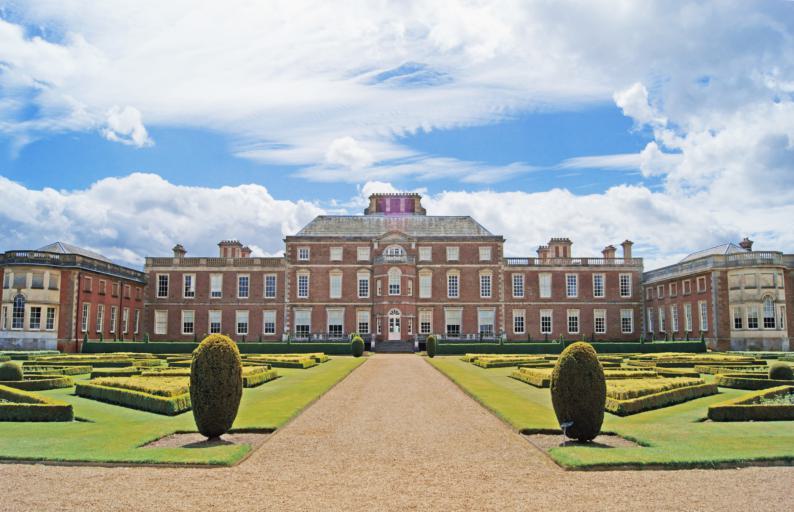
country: GB
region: England
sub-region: Cambridgeshire
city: Wimpole
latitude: 52.1418
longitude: -0.0500
